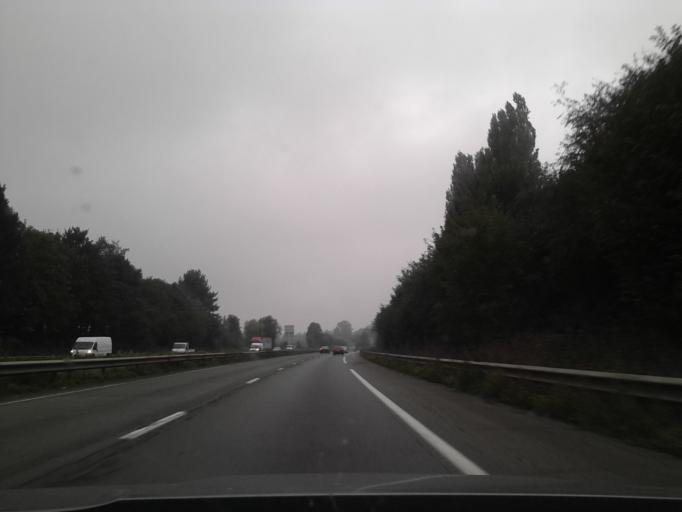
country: FR
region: Nord-Pas-de-Calais
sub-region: Departement du Nord
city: Saultain
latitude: 50.3395
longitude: 3.5639
